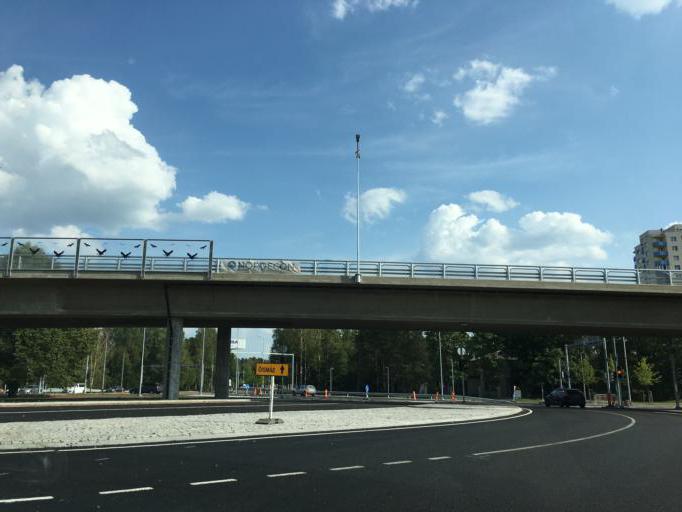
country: EE
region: Harju
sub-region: Saue vald
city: Laagri
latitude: 59.4234
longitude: 24.6456
